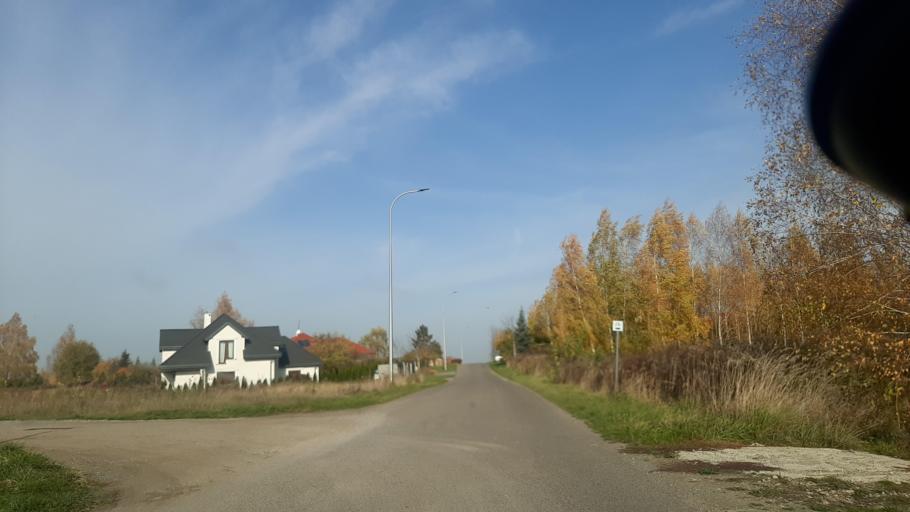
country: PL
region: Lublin Voivodeship
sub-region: Powiat lubelski
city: Lublin
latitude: 51.3213
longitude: 22.5405
